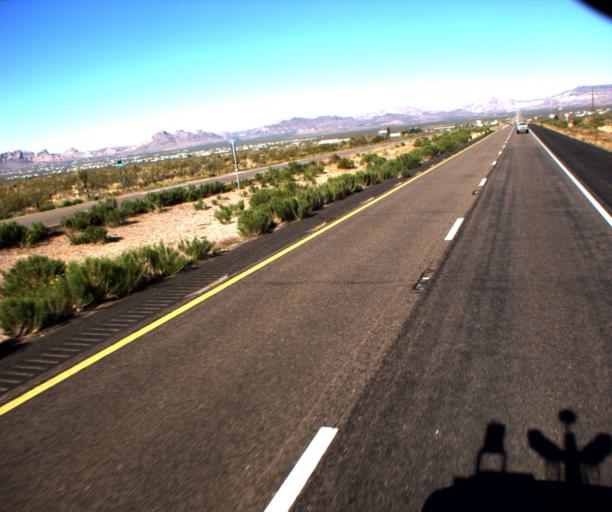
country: US
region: Arizona
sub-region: Mohave County
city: Golden Valley
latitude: 35.2243
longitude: -114.2612
